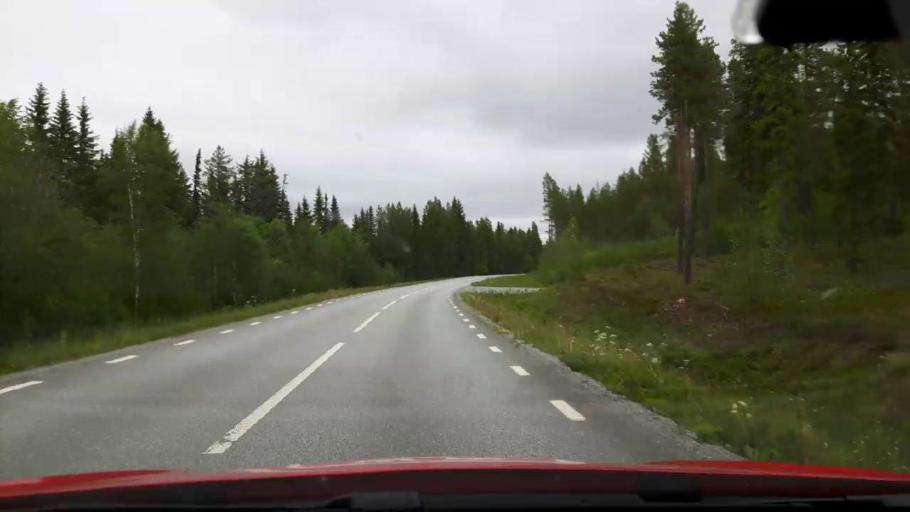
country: SE
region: Jaemtland
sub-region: OEstersunds Kommun
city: Lit
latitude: 63.7304
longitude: 14.7276
